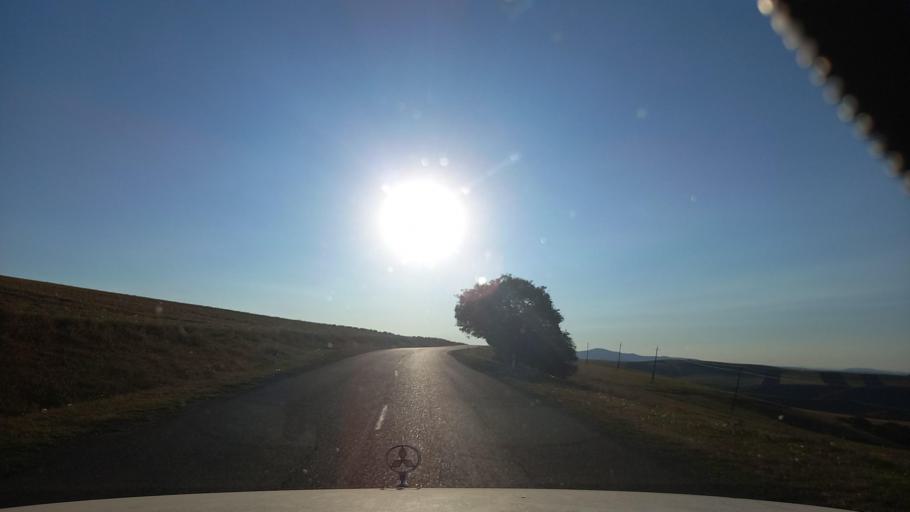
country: AZ
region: Shamkir Rayon
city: Shamkhor
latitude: 40.7658
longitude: 45.9432
